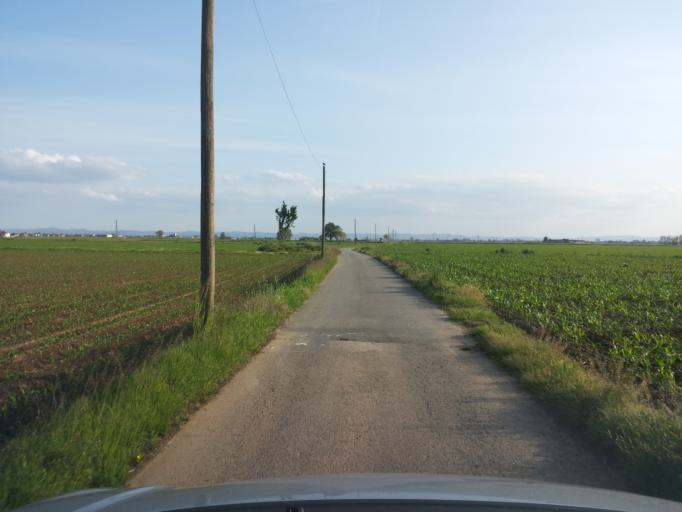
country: IT
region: Piedmont
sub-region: Provincia di Vercelli
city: Bianze
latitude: 45.3282
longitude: 8.1083
